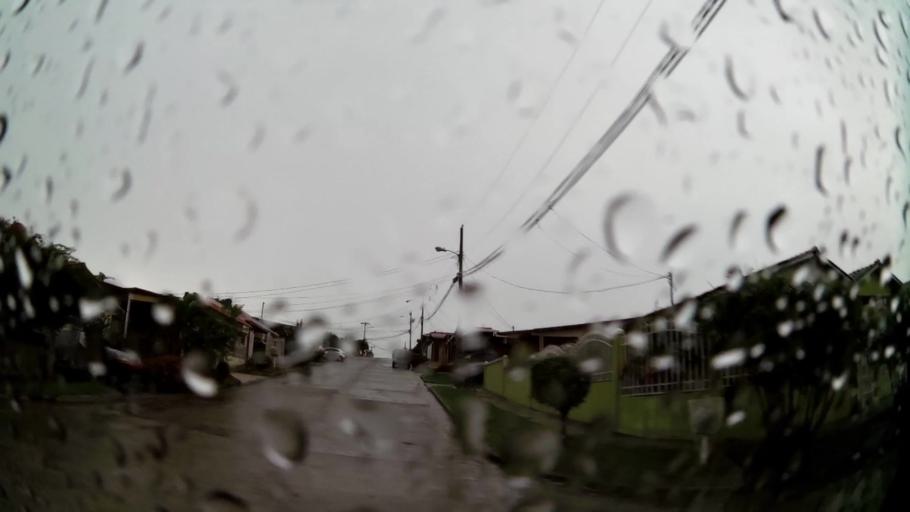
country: PA
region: Panama
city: San Miguelito
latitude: 9.0553
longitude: -79.4742
